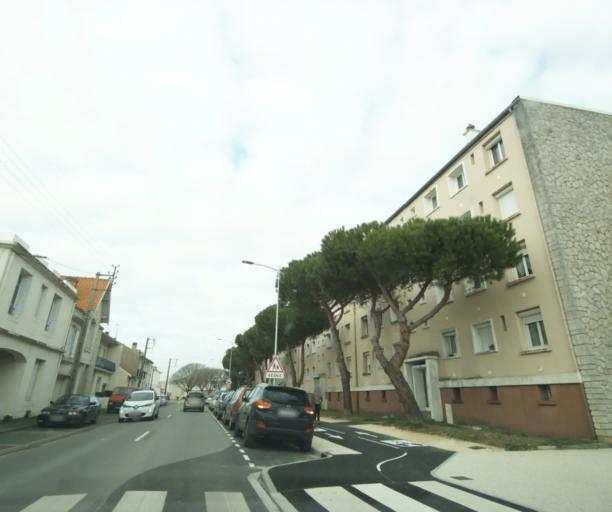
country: FR
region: Poitou-Charentes
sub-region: Departement de la Charente-Maritime
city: La Rochelle
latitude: 46.1687
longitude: -1.1637
